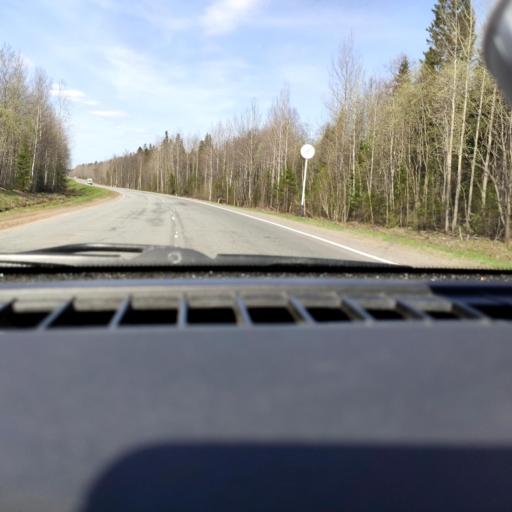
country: RU
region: Perm
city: Polazna
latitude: 58.2634
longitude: 56.1680
